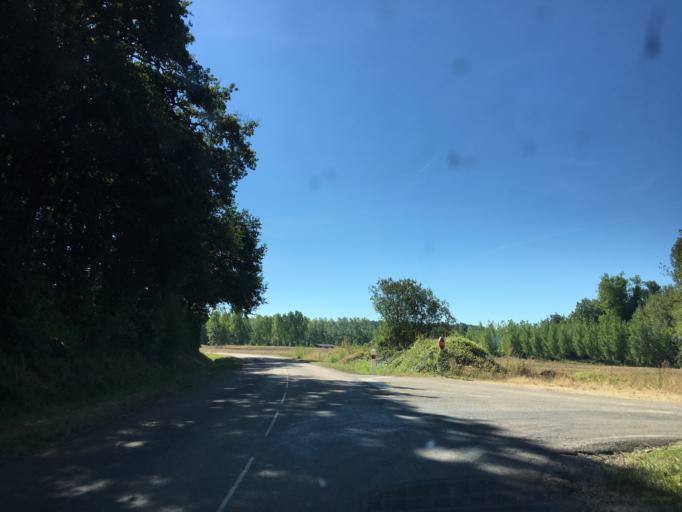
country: FR
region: Bourgogne
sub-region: Departement de l'Yonne
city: Fleury-la-Vallee
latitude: 47.8781
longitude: 3.4454
